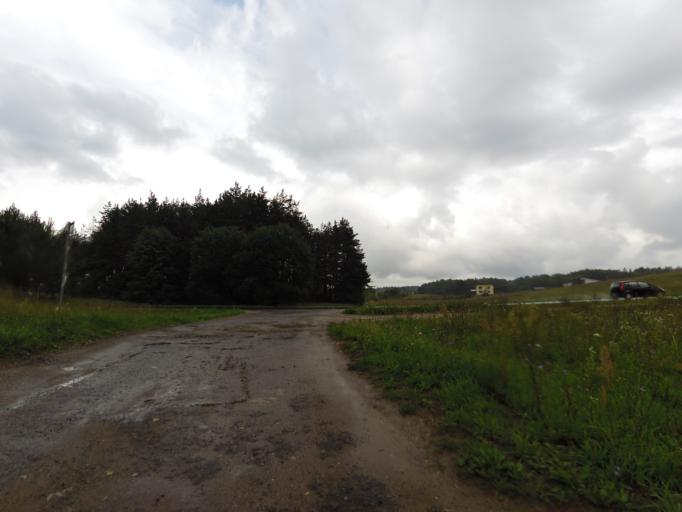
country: LT
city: Grigiskes
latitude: 54.7172
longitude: 25.1136
